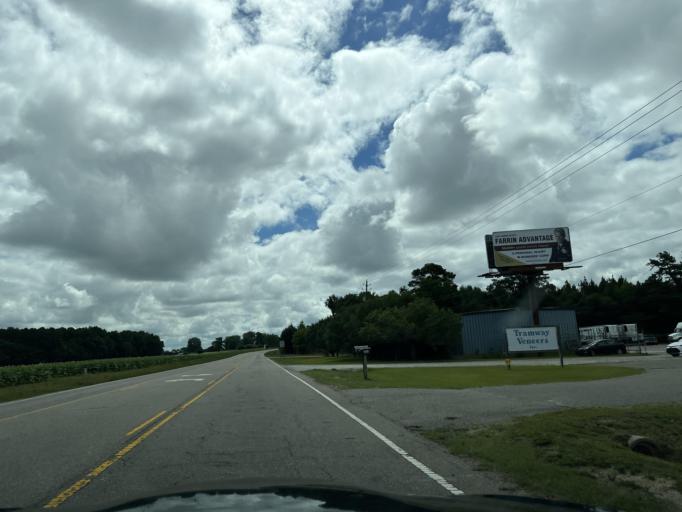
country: US
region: North Carolina
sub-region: Lee County
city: Sanford
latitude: 35.4376
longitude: -79.1991
